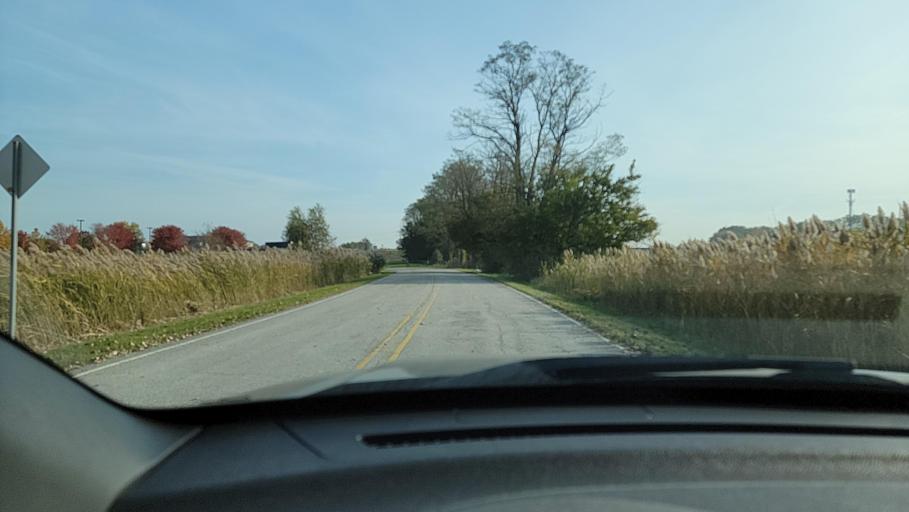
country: US
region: Indiana
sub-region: Porter County
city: Ogden Dunes
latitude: 41.6025
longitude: -87.1776
